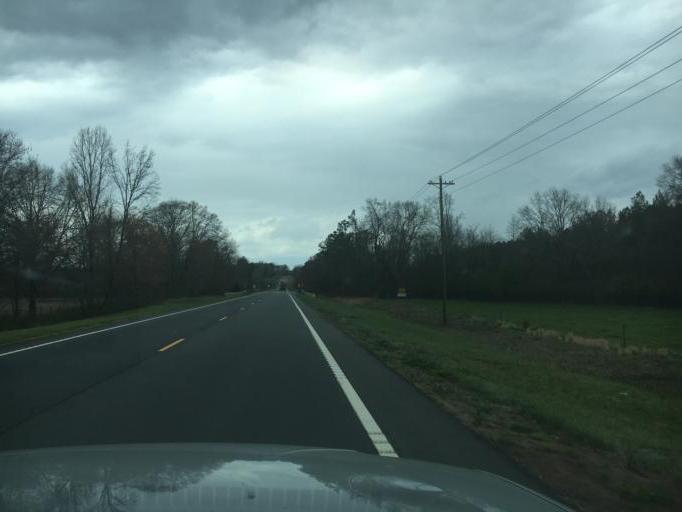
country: US
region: South Carolina
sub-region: Oconee County
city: Walhalla
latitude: 34.7903
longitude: -83.0226
